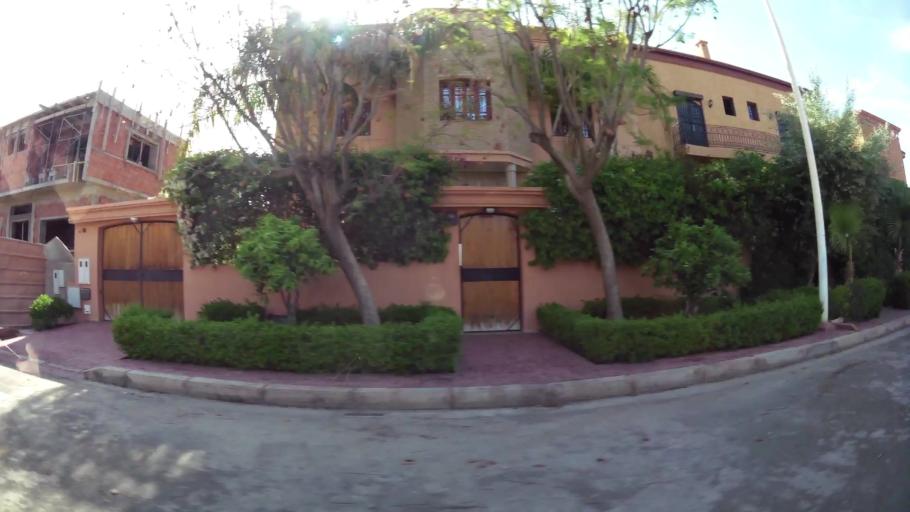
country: MA
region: Marrakech-Tensift-Al Haouz
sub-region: Marrakech
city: Marrakesh
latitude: 31.6526
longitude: -8.0441
